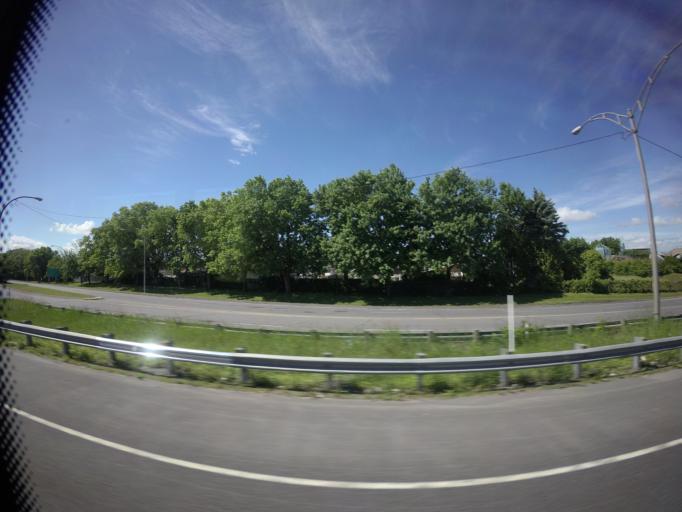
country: CA
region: Quebec
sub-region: Monteregie
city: Boucherville
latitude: 45.5779
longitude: -73.4748
